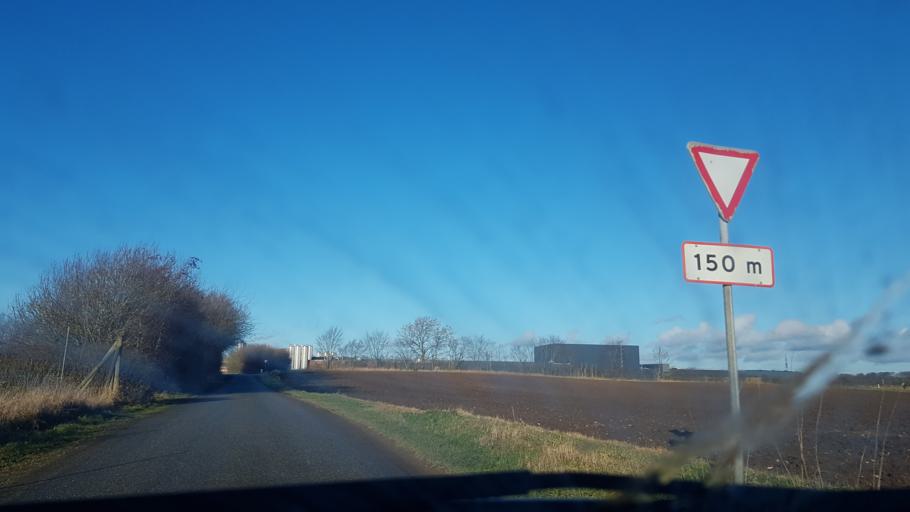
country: DK
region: South Denmark
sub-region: Fredericia Kommune
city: Taulov
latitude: 55.5304
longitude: 9.6447
